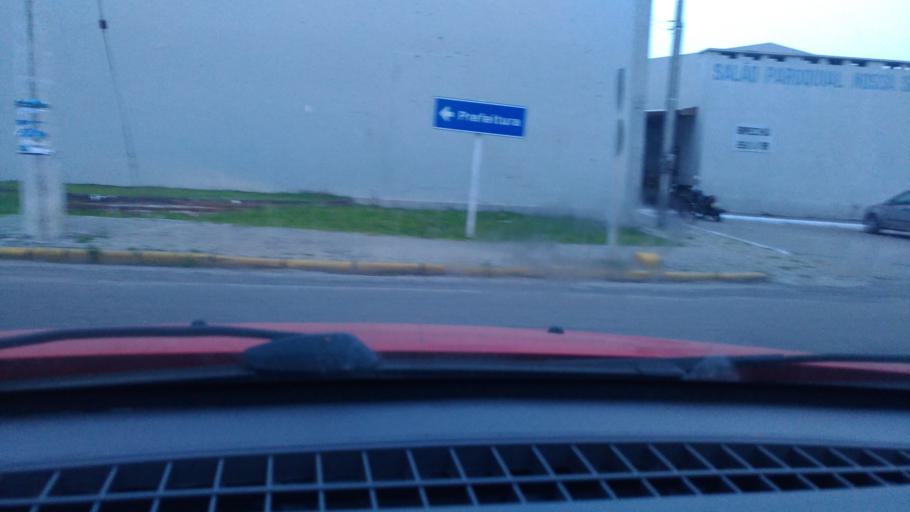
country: BR
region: Rio Grande do Sul
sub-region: Capao Da Canoa
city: Capao da Canoa
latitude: -29.8532
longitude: -50.0659
